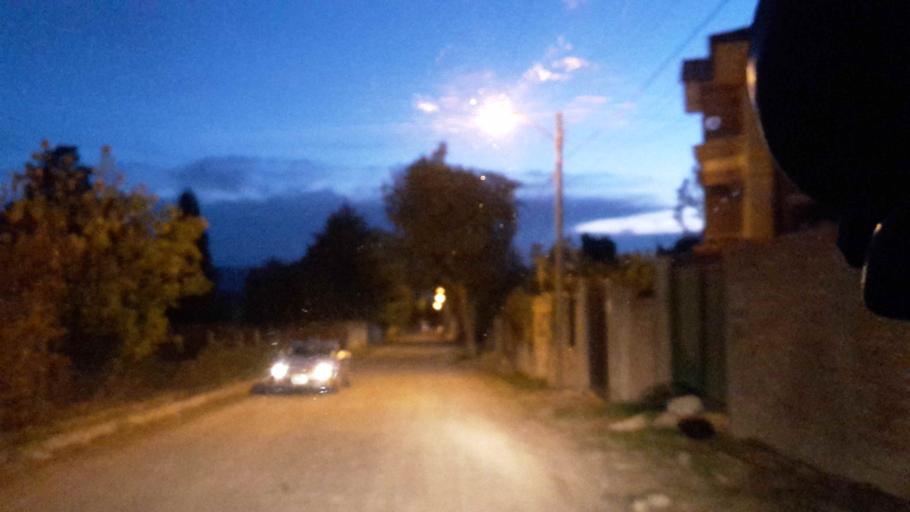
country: BO
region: Cochabamba
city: Cochabamba
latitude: -17.3297
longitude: -66.2172
